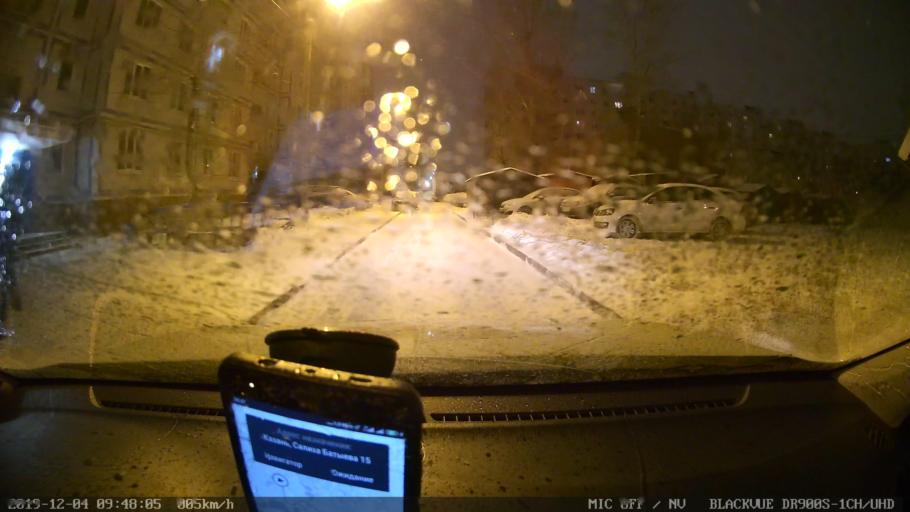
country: RU
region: Tatarstan
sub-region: Gorod Kazan'
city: Kazan
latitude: 55.8396
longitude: 49.1314
